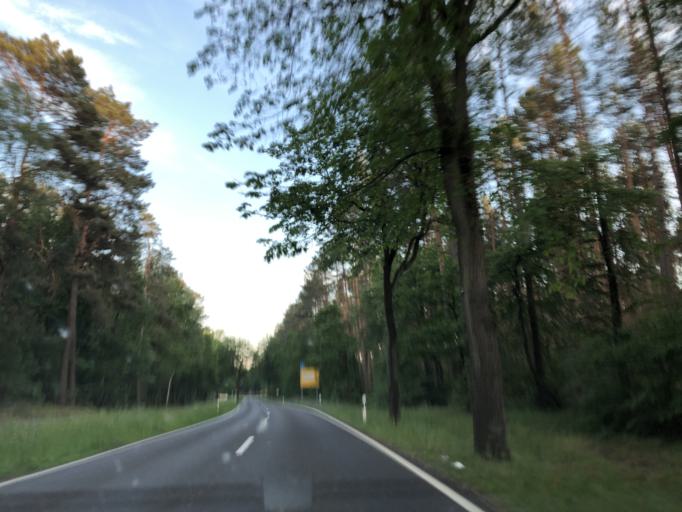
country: DE
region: Brandenburg
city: Bernau bei Berlin
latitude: 52.7094
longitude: 13.5356
